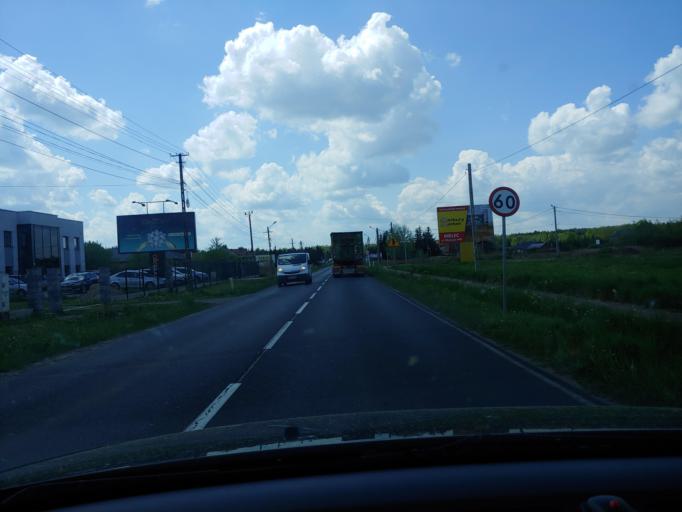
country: PL
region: Subcarpathian Voivodeship
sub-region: Powiat mielecki
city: Trzciana
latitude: 50.2744
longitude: 21.3736
